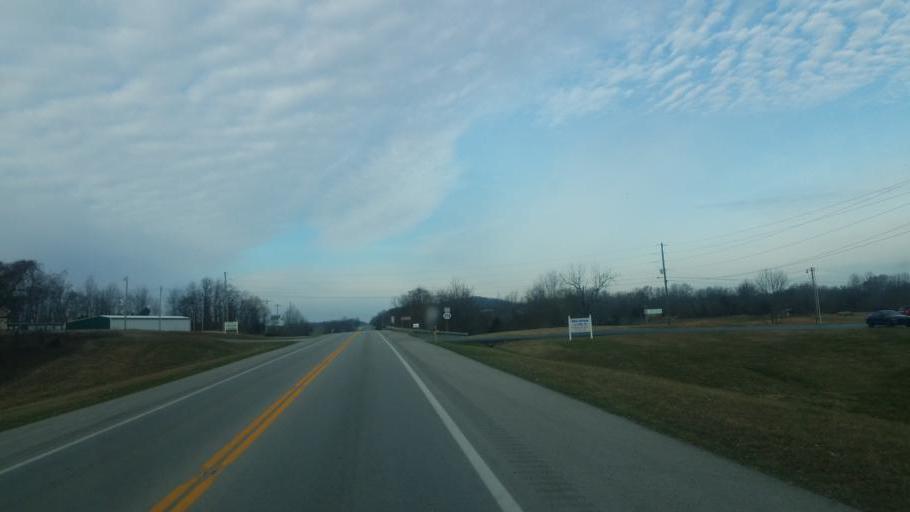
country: US
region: Kentucky
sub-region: Clinton County
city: Albany
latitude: 36.7551
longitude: -85.1448
